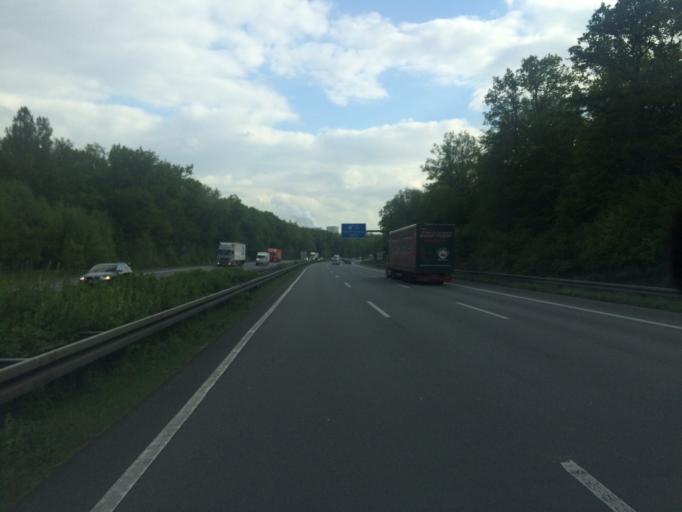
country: DE
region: North Rhine-Westphalia
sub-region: Regierungsbezirk Munster
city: Beckum
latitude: 51.7089
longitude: 7.9786
